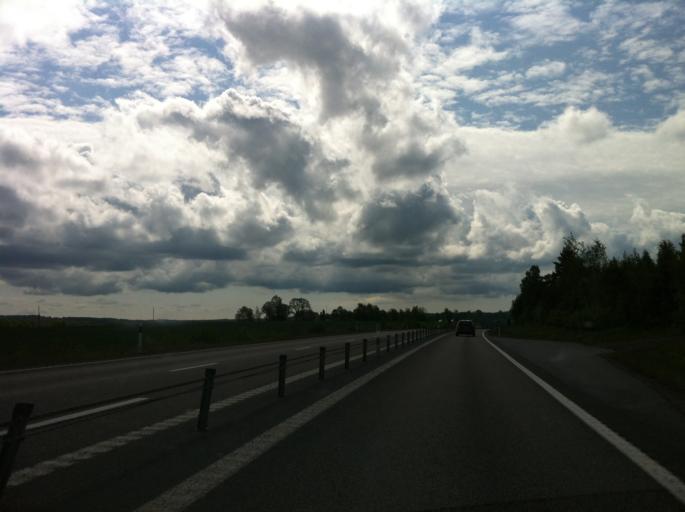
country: SE
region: Vaermland
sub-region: Karlstads Kommun
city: Edsvalla
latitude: 59.5450
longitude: 13.1987
